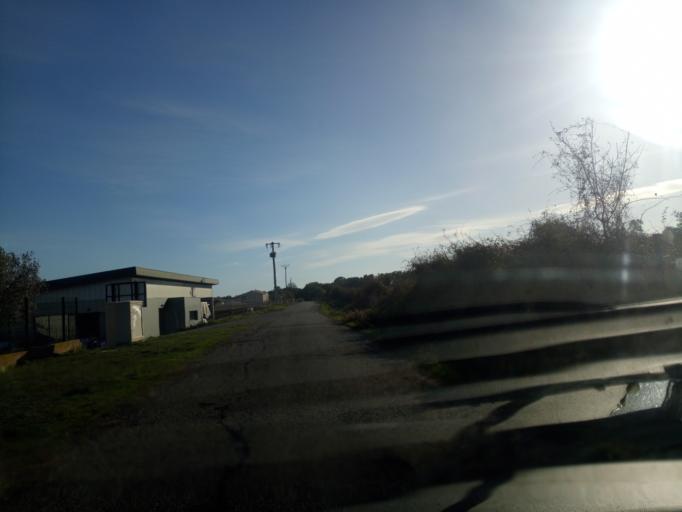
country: FR
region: Corsica
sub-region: Departement de la Haute-Corse
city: Linguizzetta
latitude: 42.2629
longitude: 9.5444
